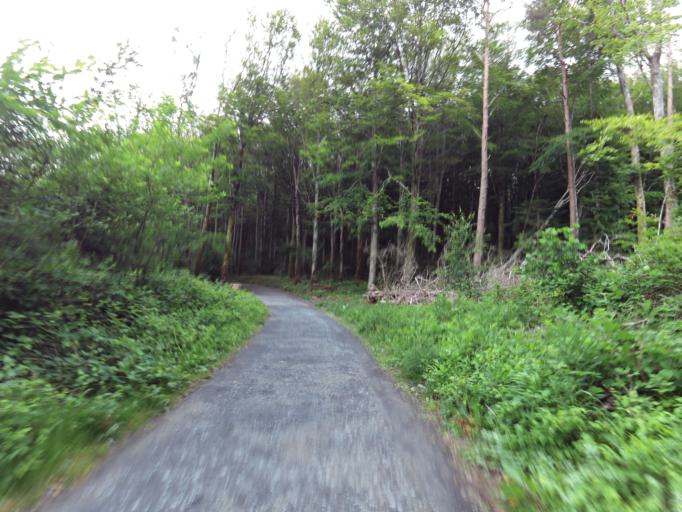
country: IE
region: Connaught
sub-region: County Galway
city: Gort
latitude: 53.0858
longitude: -8.8462
